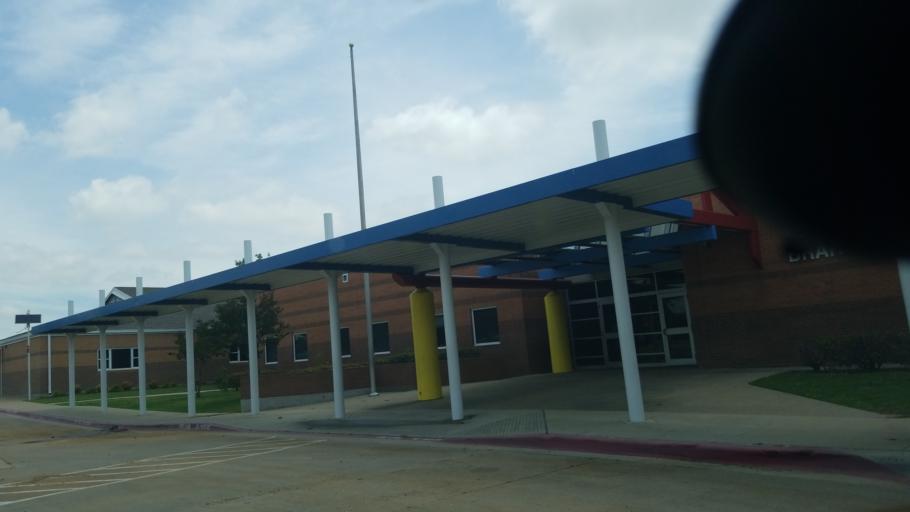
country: US
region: Texas
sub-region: Dallas County
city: Irving
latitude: 32.8450
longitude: -96.9658
